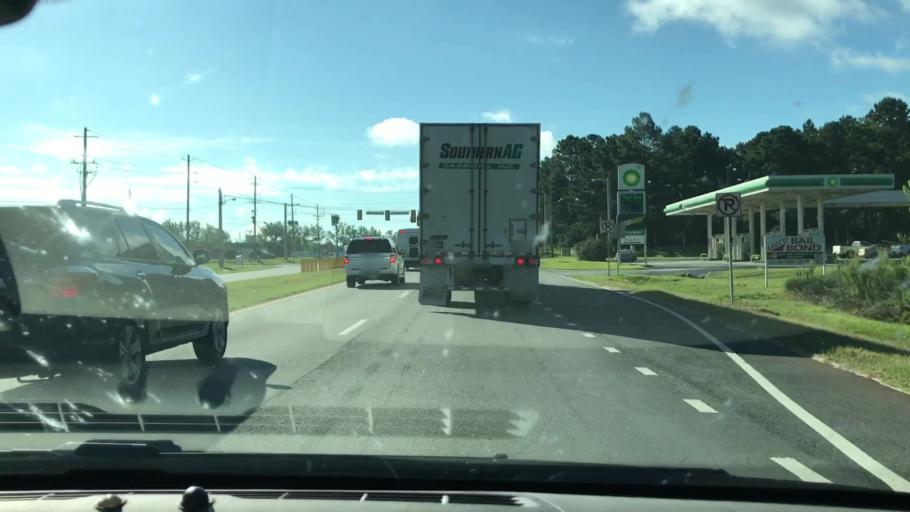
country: US
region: Georgia
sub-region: Dougherty County
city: Albany
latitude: 31.6366
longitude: -84.2475
